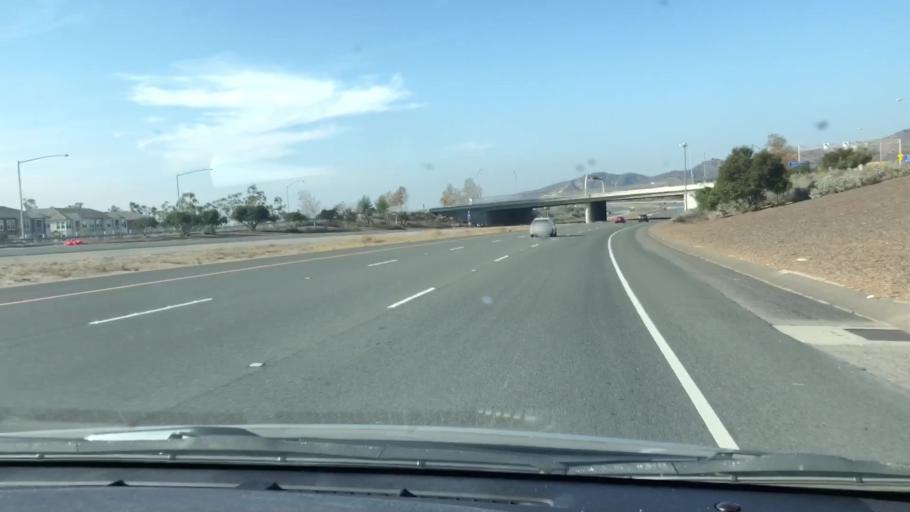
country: US
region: California
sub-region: Orange County
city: Foothill Ranch
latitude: 33.6782
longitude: -117.6720
